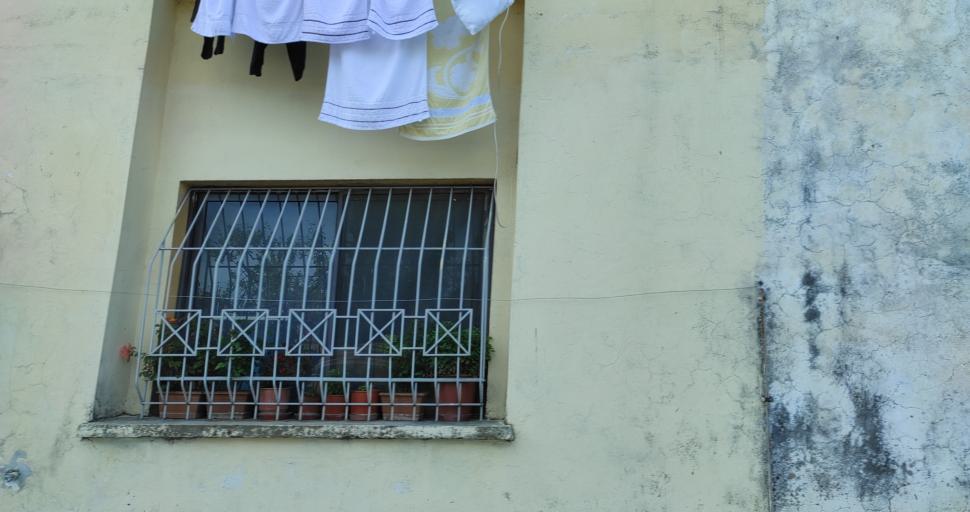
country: AL
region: Shkoder
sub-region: Rrethi i Shkodres
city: Shkoder
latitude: 42.0766
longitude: 19.5229
